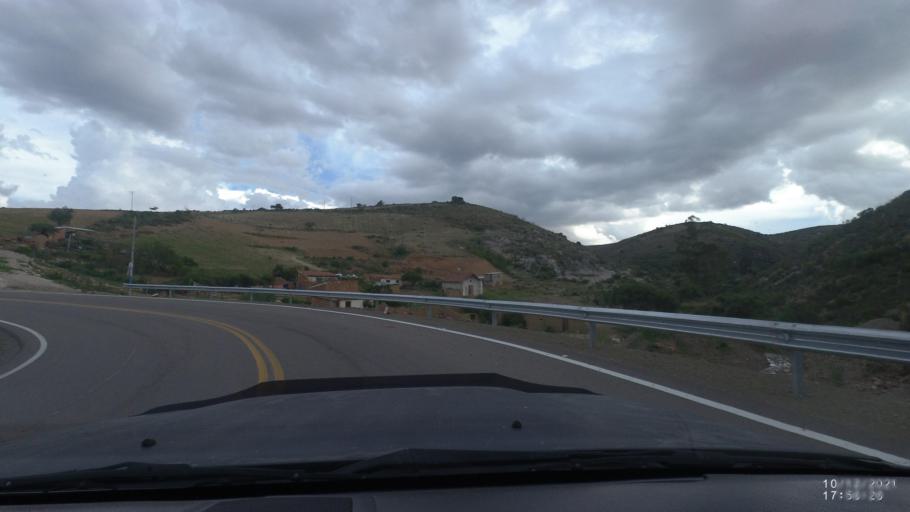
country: BO
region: Cochabamba
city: Cliza
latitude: -17.7159
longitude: -65.9381
